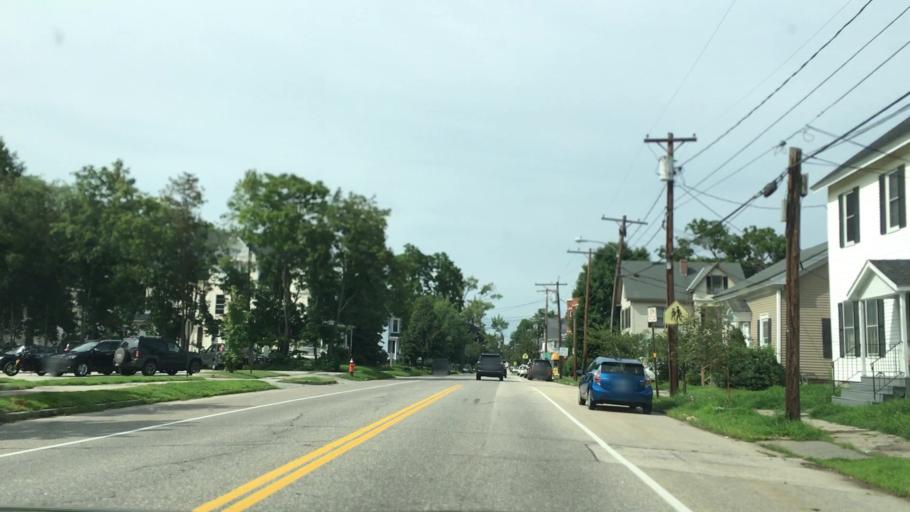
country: US
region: New Hampshire
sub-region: Merrimack County
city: Concord
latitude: 43.1963
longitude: -71.5393
